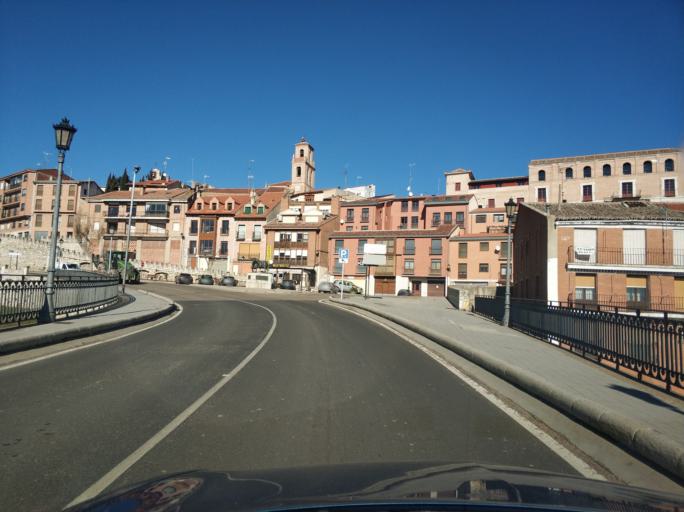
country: ES
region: Castille and Leon
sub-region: Provincia de Valladolid
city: Tordesillas
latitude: 41.4988
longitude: -5.0011
